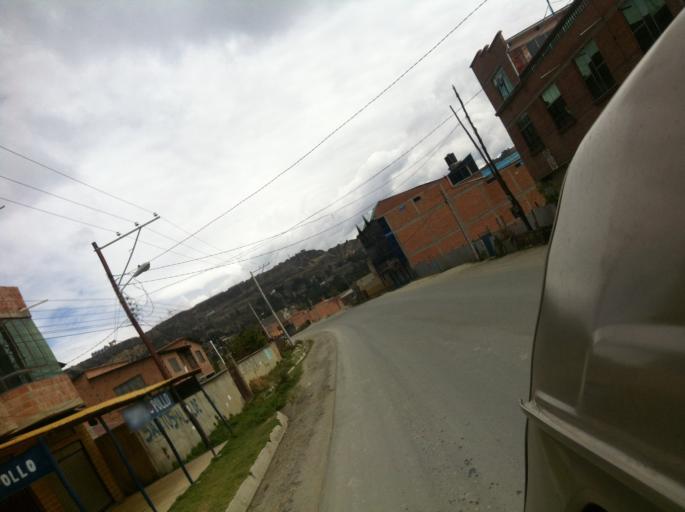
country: BO
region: La Paz
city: La Paz
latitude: -16.5764
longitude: -68.1691
